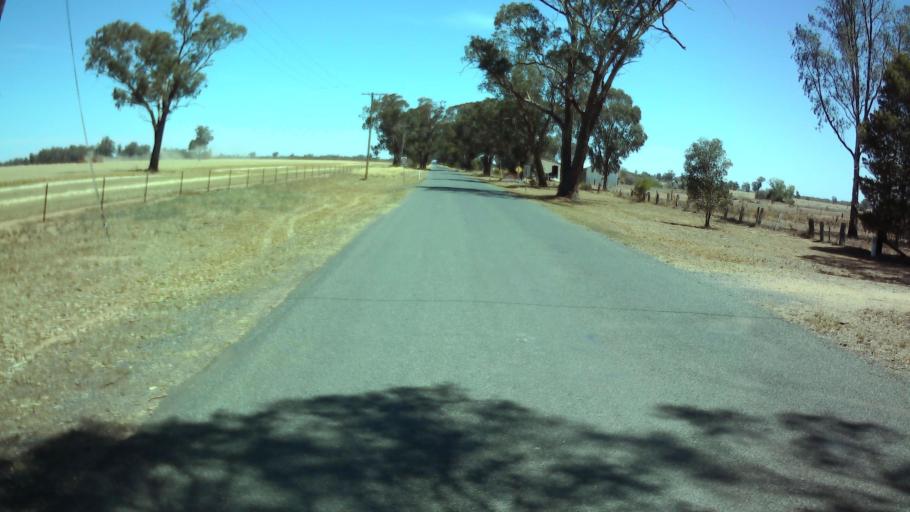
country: AU
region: New South Wales
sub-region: Weddin
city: Grenfell
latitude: -34.0148
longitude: 147.7939
